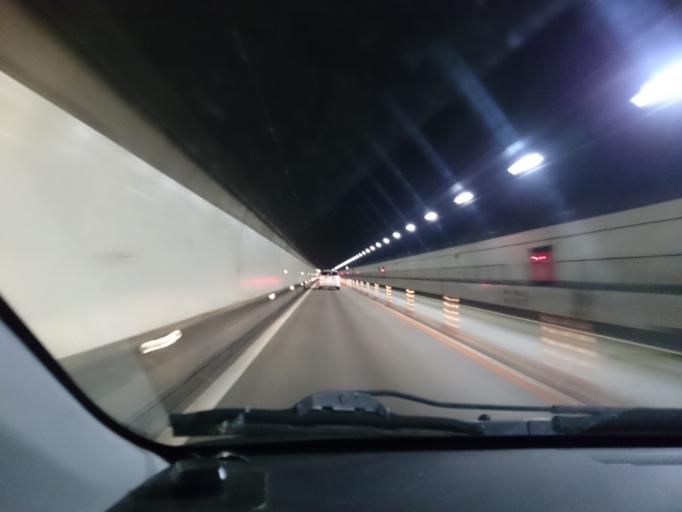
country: JP
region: Fukushima
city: Kitakata
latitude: 37.5472
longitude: 139.7901
